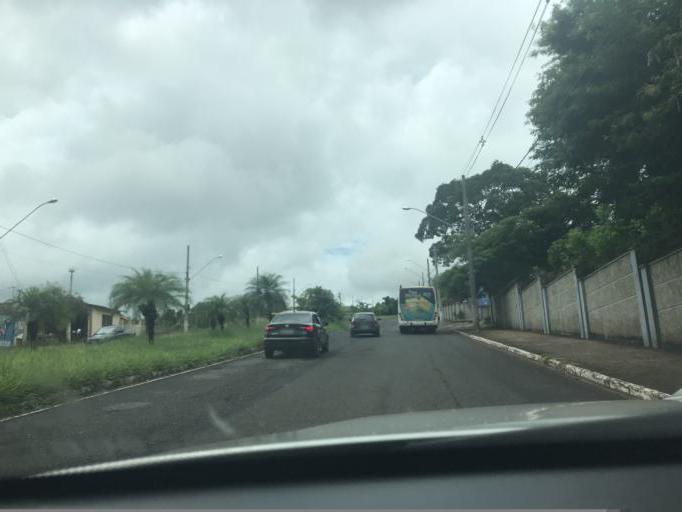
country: BR
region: Minas Gerais
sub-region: Araxa
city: Araxa
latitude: -19.5808
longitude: -46.9410
